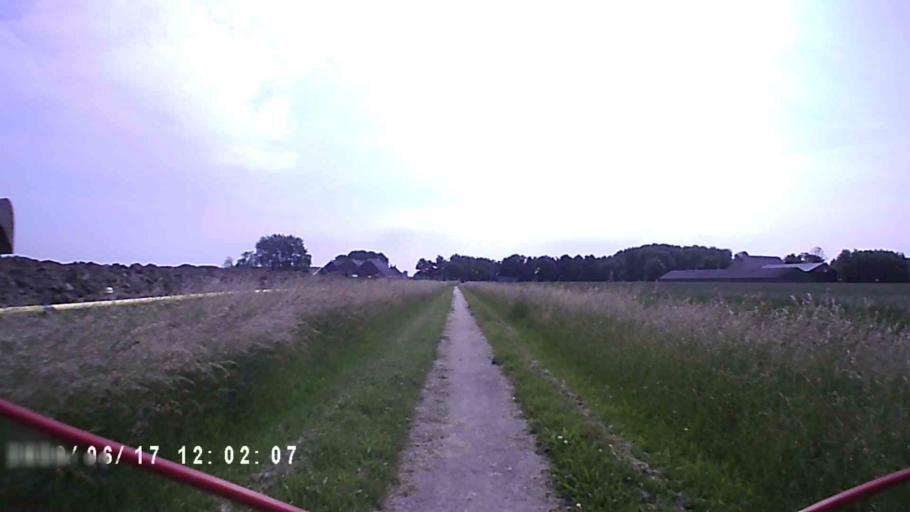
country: NL
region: Groningen
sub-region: Gemeente De Marne
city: Ulrum
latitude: 53.3405
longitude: 6.3385
